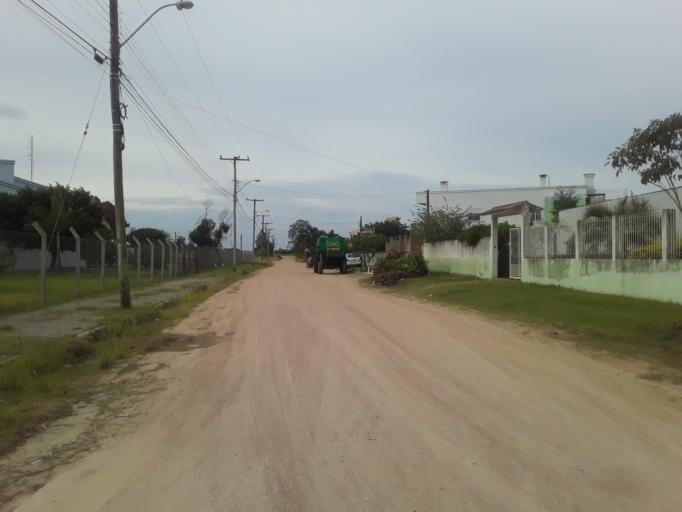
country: BR
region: Rio Grande do Sul
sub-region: Sao Lourenco Do Sul
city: Sao Lourenco do Sul
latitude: -31.3564
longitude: -51.9878
